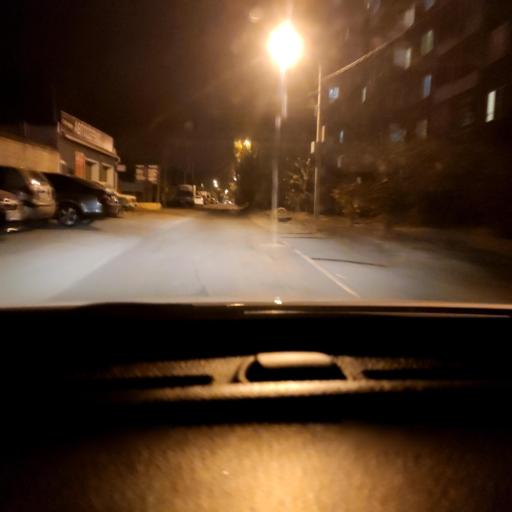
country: RU
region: Voronezj
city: Maslovka
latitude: 51.6393
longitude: 39.2746
